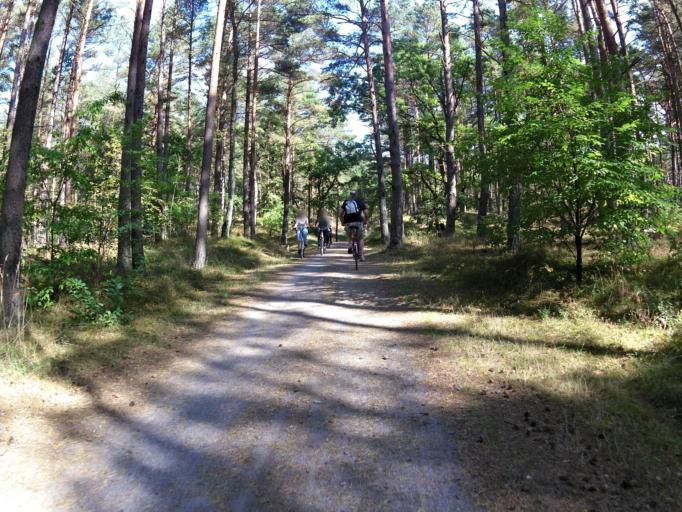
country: DE
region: Mecklenburg-Vorpommern
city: Karlshagen
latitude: 54.1095
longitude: 13.8519
